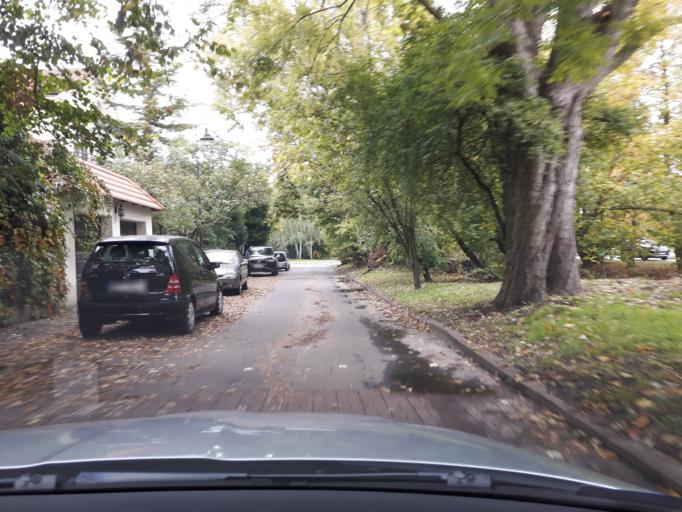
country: PL
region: Masovian Voivodeship
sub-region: Warszawa
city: Mokotow
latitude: 52.1883
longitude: 21.0338
